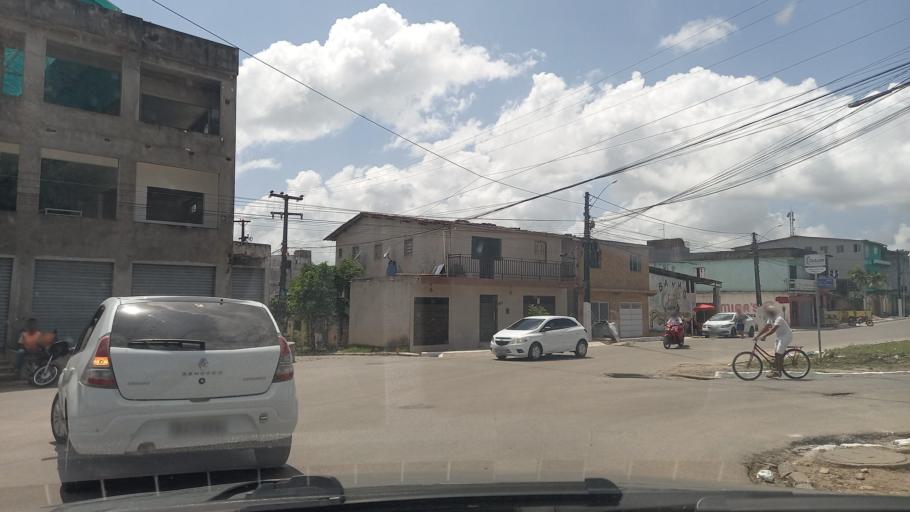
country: BR
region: Pernambuco
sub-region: Goiana
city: Goiana
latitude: -7.5597
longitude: -35.0116
